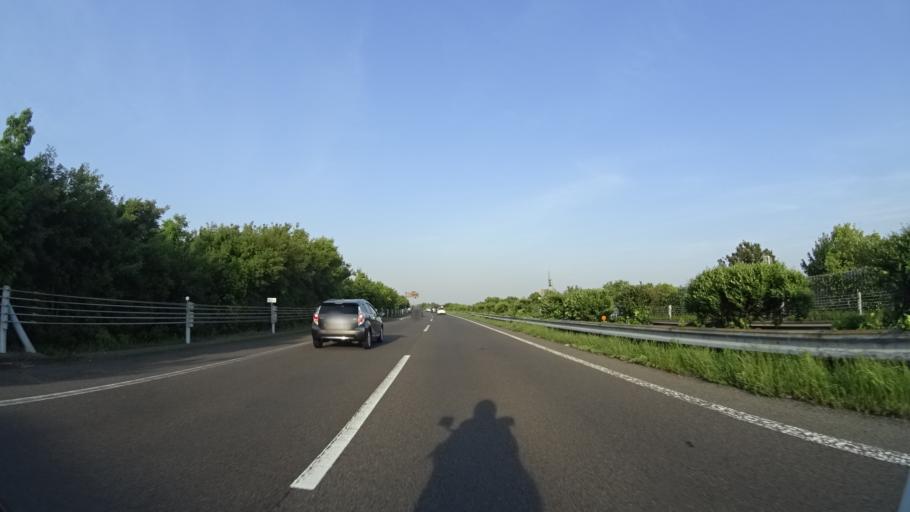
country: JP
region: Kagawa
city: Marugame
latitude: 34.2415
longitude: 133.7781
